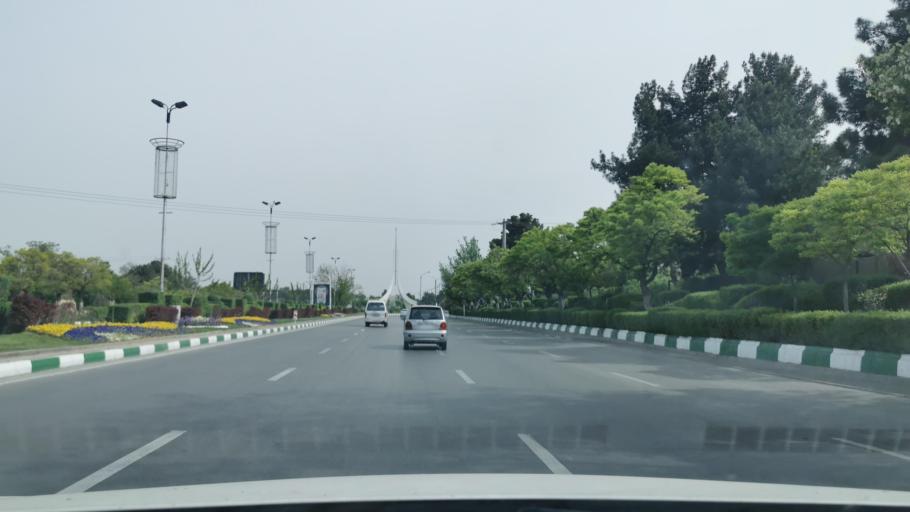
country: IR
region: Razavi Khorasan
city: Mashhad
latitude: 36.2457
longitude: 59.6210
